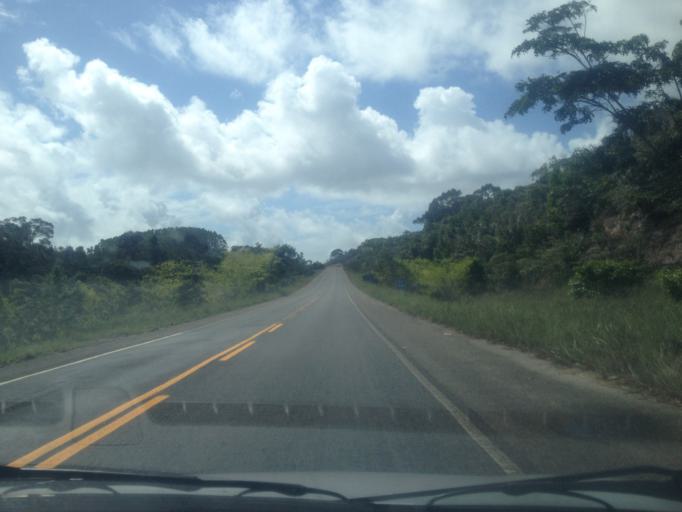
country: BR
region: Bahia
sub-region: Conde
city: Conde
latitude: -12.0254
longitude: -37.6953
